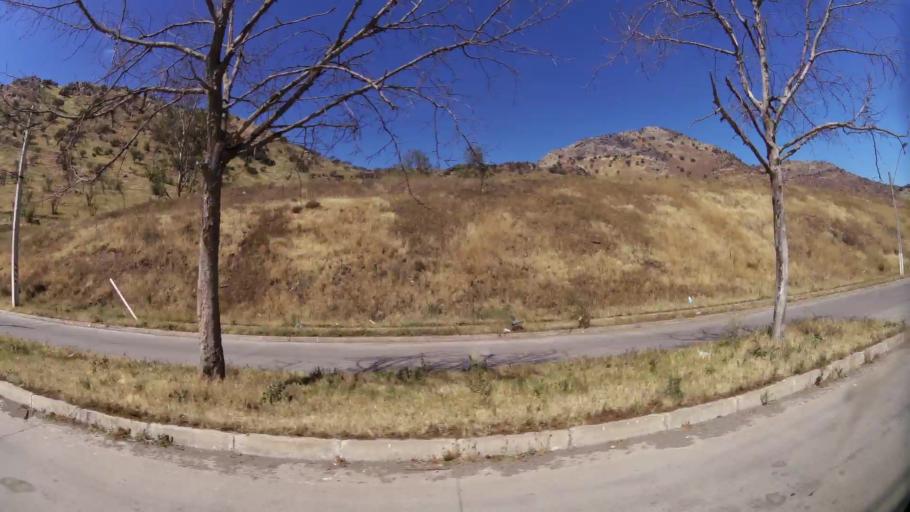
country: CL
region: Santiago Metropolitan
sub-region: Provincia de Santiago
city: Lo Prado
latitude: -33.3812
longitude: -70.7403
